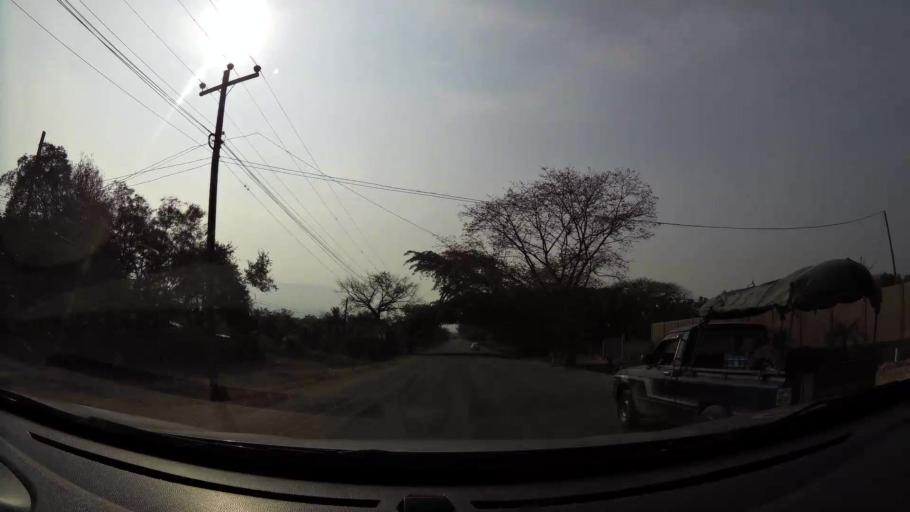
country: HN
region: Comayagua
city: Comayagua
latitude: 14.4580
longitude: -87.6592
